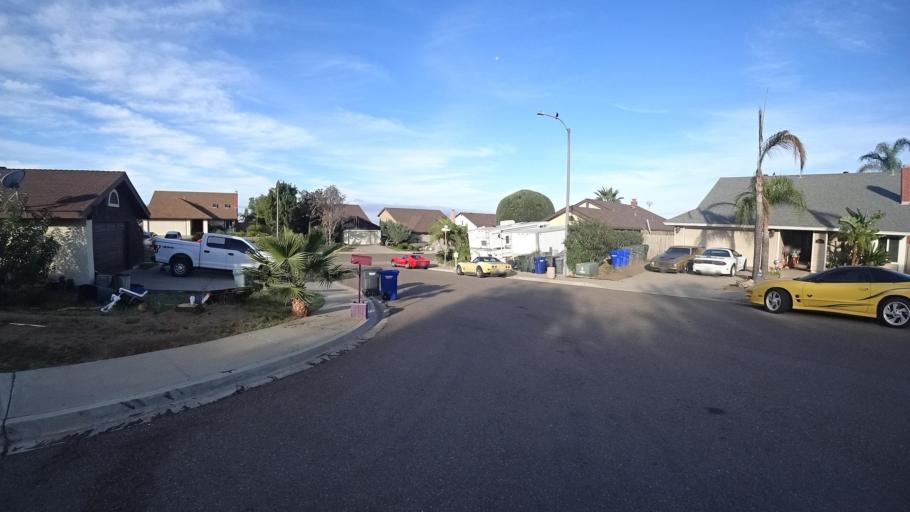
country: US
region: California
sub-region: San Diego County
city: Spring Valley
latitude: 32.7284
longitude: -116.9981
